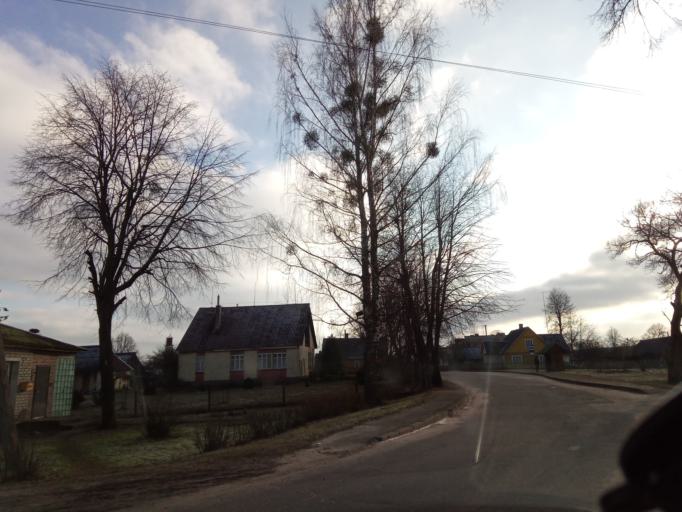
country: LT
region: Alytaus apskritis
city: Druskininkai
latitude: 53.9519
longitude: 24.2944
